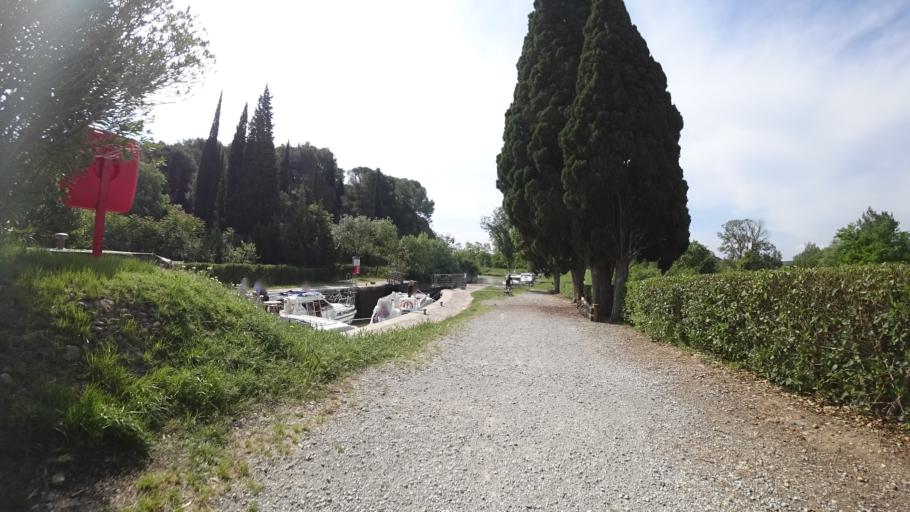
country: FR
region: Languedoc-Roussillon
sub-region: Departement de l'Herault
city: Olonzac
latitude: 43.2501
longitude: 2.7569
